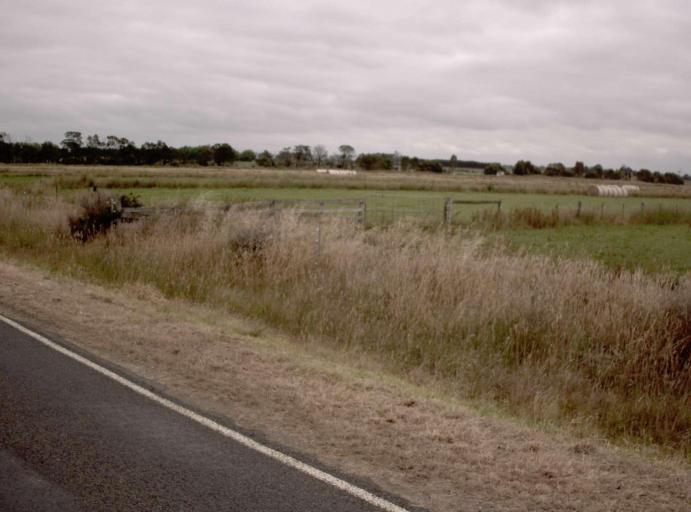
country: AU
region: Victoria
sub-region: Wellington
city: Sale
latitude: -38.0617
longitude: 146.9714
